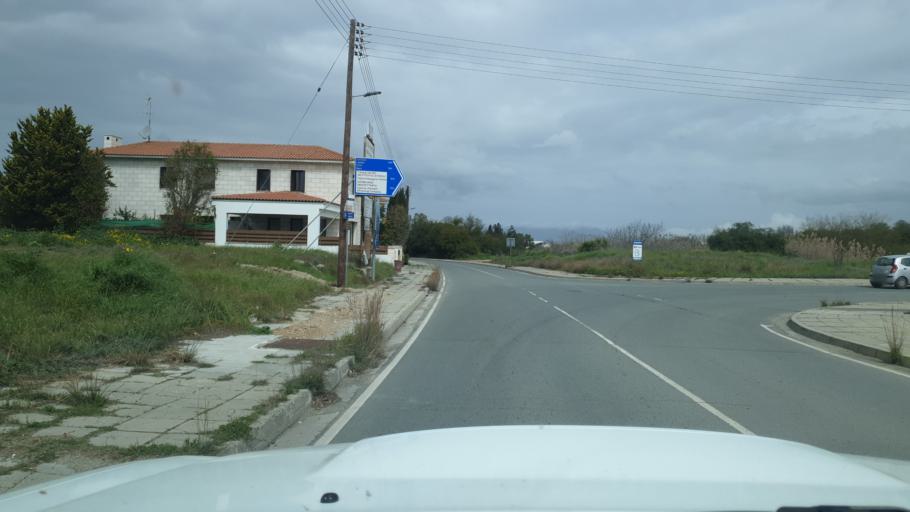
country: CY
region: Lefkosia
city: Tseri
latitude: 35.1053
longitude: 33.3562
